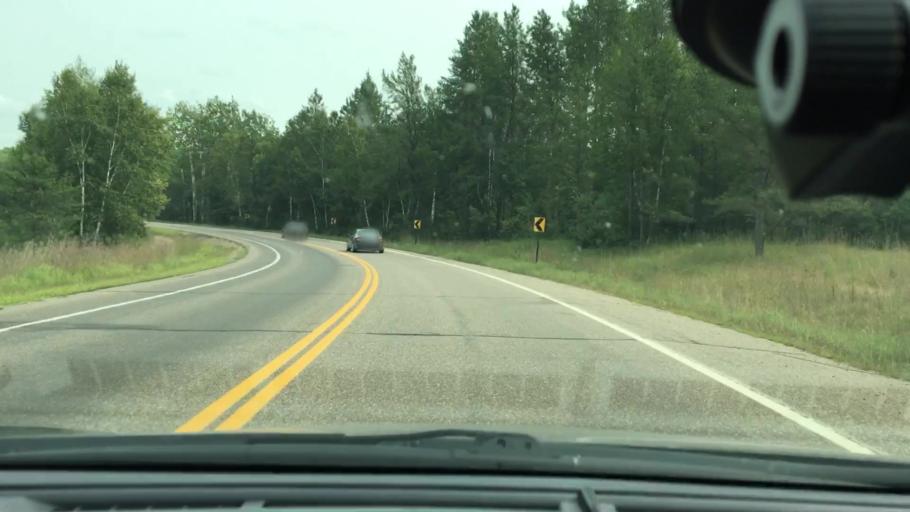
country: US
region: Minnesota
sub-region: Crow Wing County
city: Cross Lake
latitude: 46.7316
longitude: -94.0283
